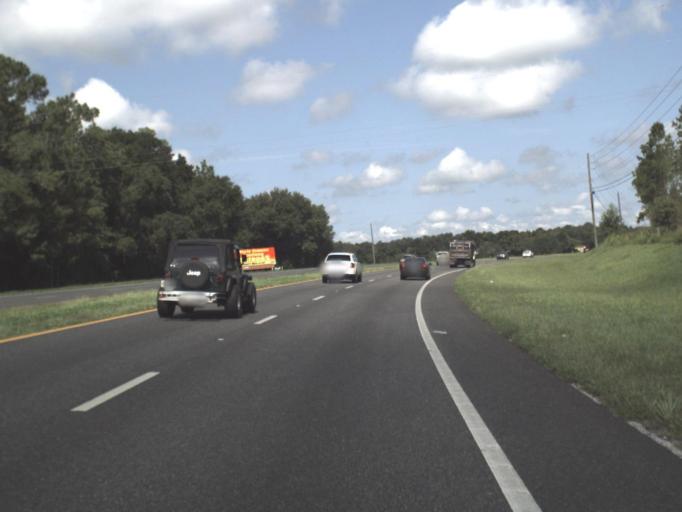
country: US
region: Florida
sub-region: Hernando County
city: Hill 'n Dale
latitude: 28.5234
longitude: -82.3077
